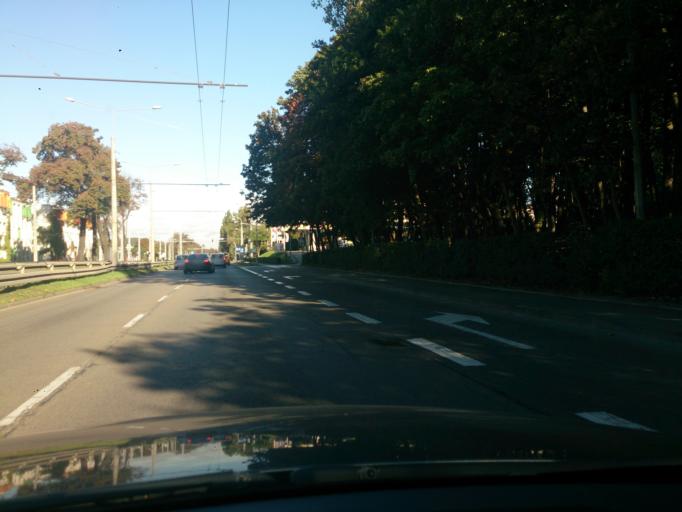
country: PL
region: Pomeranian Voivodeship
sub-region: Gdynia
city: Gdynia
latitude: 54.4954
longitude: 18.5390
